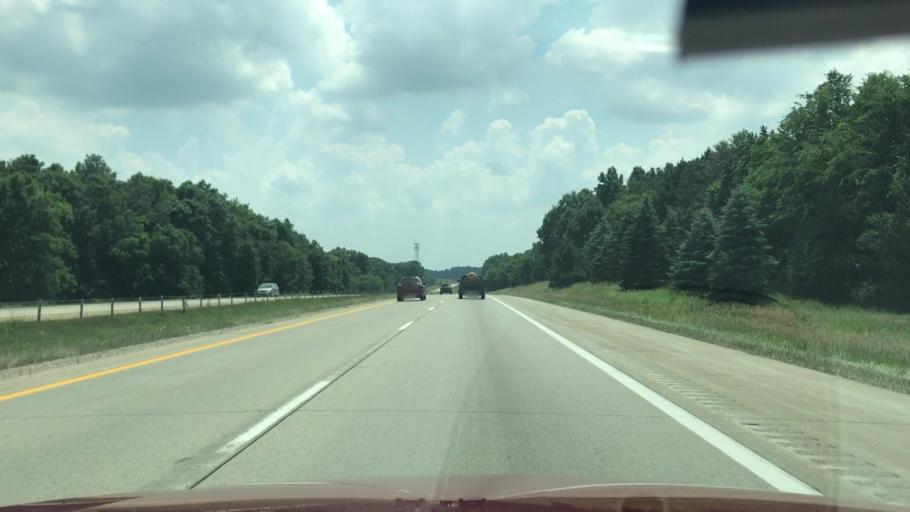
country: US
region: Michigan
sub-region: Allegan County
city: Otsego
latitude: 42.5045
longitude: -85.6539
